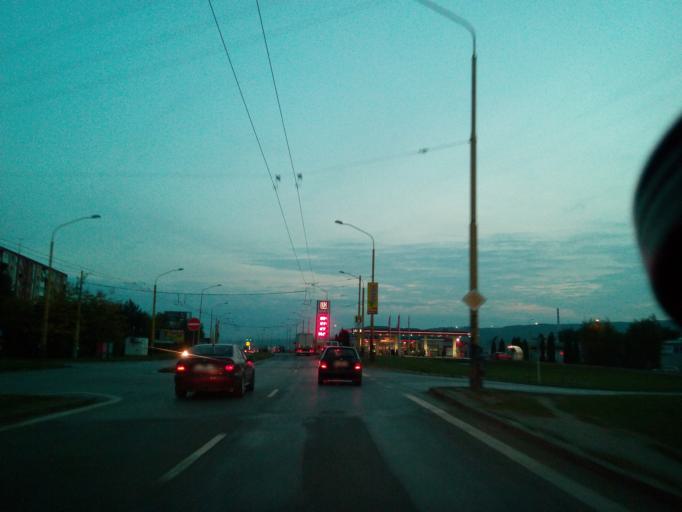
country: SK
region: Presovsky
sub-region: Okres Presov
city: Presov
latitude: 48.9933
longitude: 21.2670
